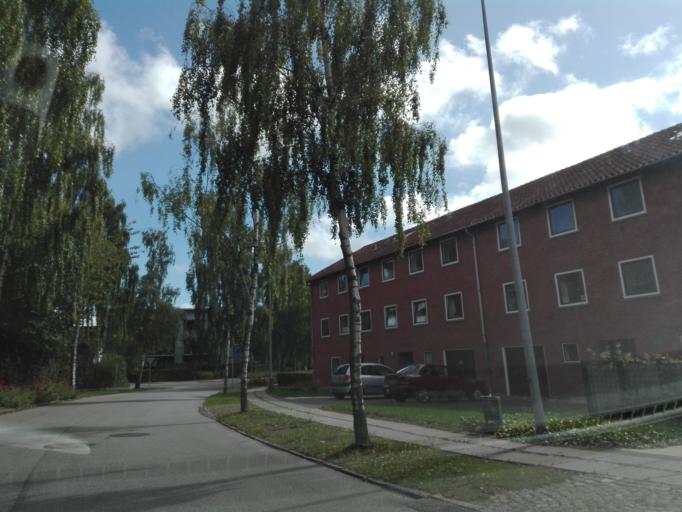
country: DK
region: Central Jutland
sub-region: Arhus Kommune
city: Arhus
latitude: 56.1157
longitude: 10.1931
